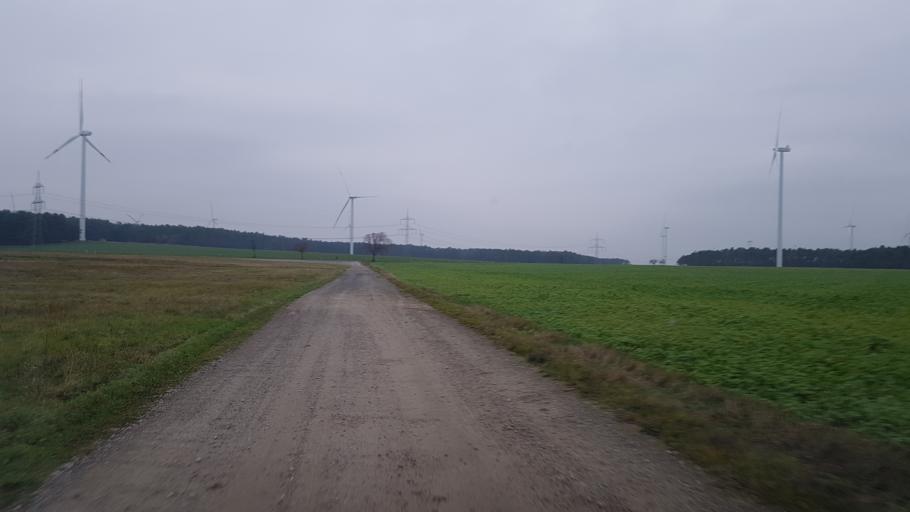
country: DE
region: Brandenburg
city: Schilda
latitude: 51.6532
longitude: 13.3775
